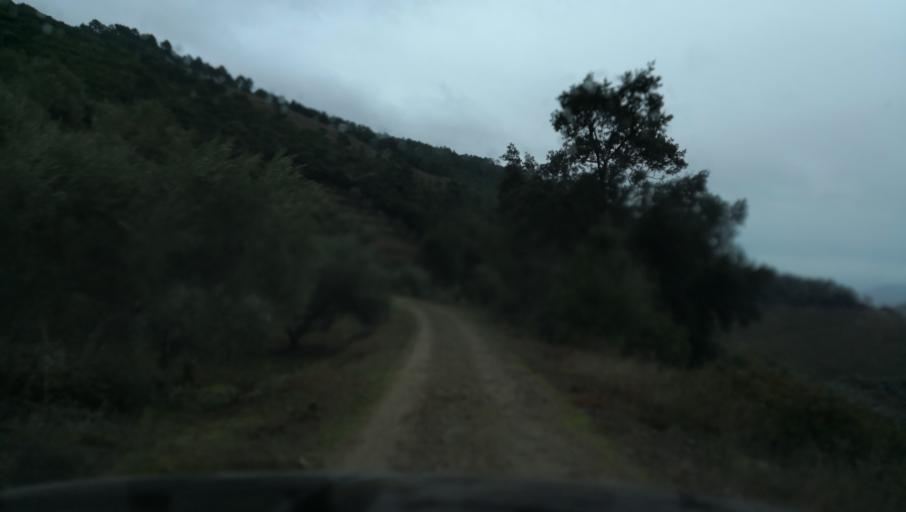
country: PT
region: Vila Real
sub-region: Vila Real
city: Vila Real
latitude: 41.2590
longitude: -7.7454
